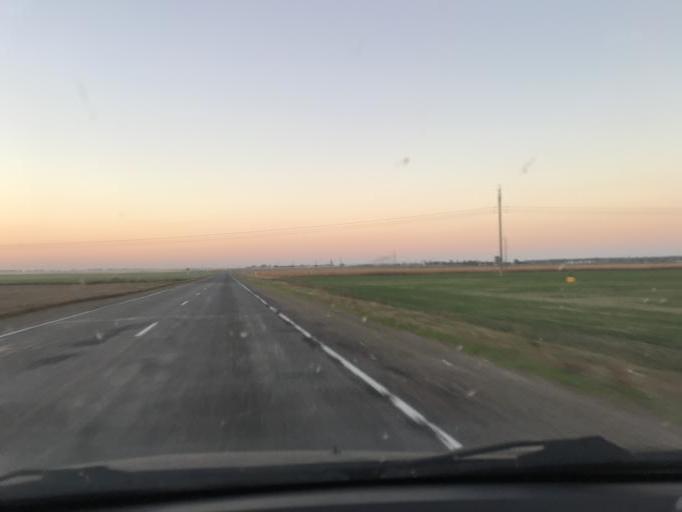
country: BY
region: Gomel
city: Horad Rechytsa
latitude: 52.2334
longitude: 30.5096
